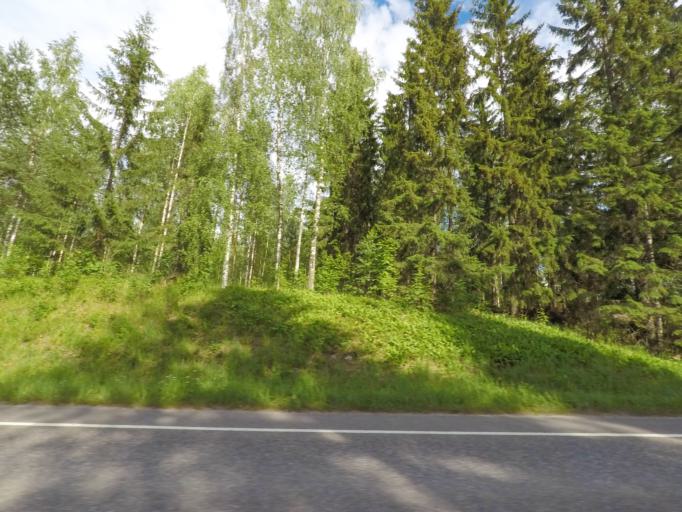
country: FI
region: Uusimaa
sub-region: Porvoo
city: Pukkila
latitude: 60.8085
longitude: 25.4807
